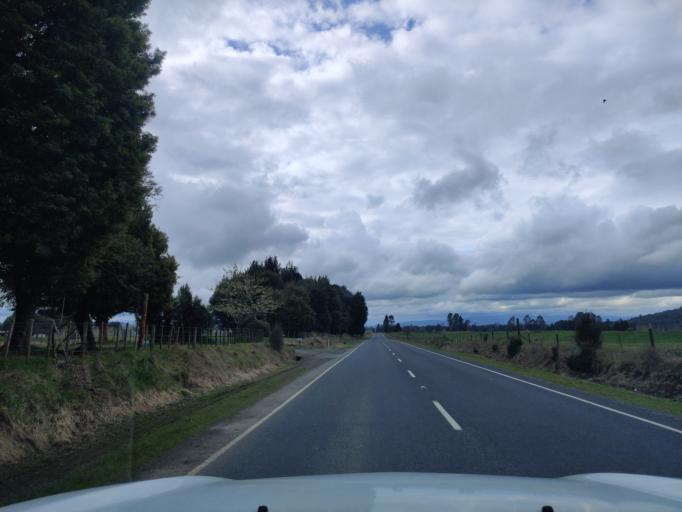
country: NZ
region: Waikato
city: Turangi
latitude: -39.0409
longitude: 175.3832
